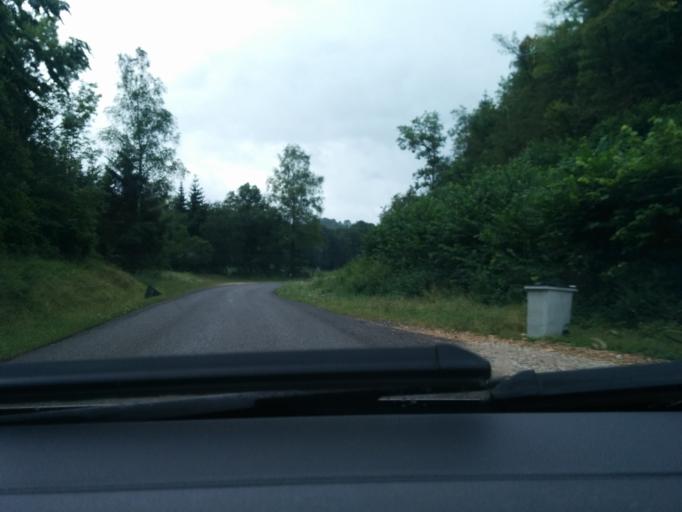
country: FR
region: Franche-Comte
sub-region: Departement du Jura
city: Saint-Lupicin
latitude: 46.4276
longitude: 5.8086
